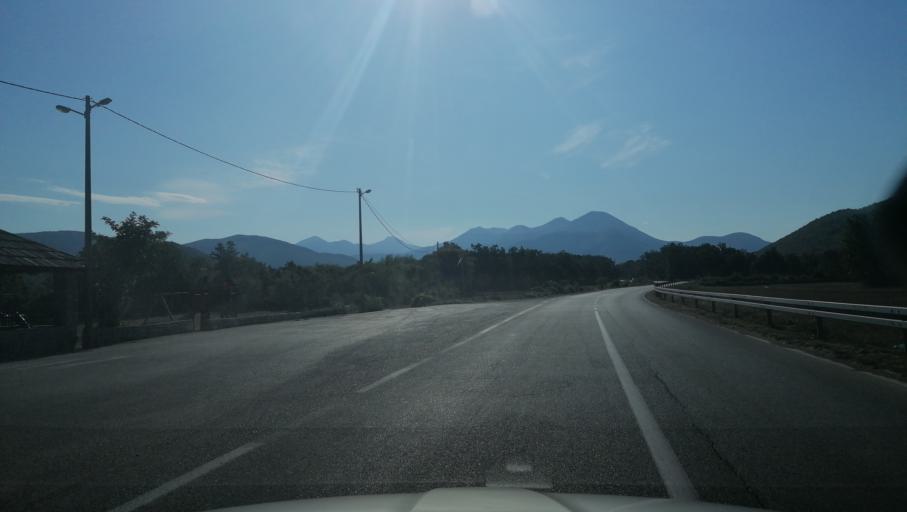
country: BA
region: Republika Srpska
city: Trebinje
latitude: 42.6473
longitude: 18.3760
